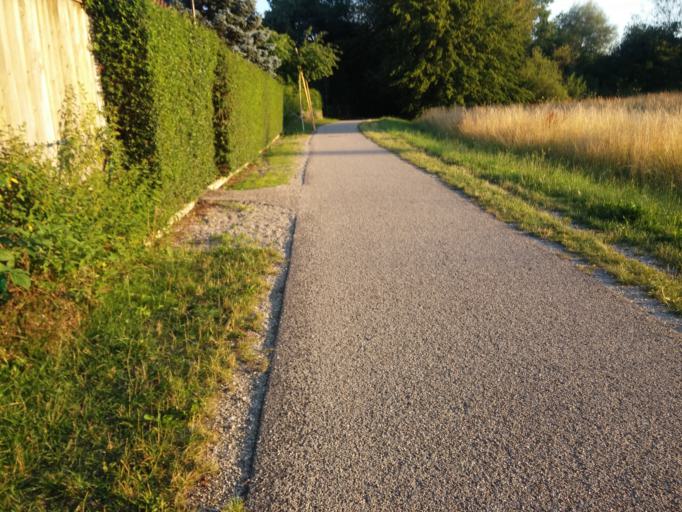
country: DE
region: Bavaria
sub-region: Upper Bavaria
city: Markt Schwaben
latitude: 48.1964
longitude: 11.8729
